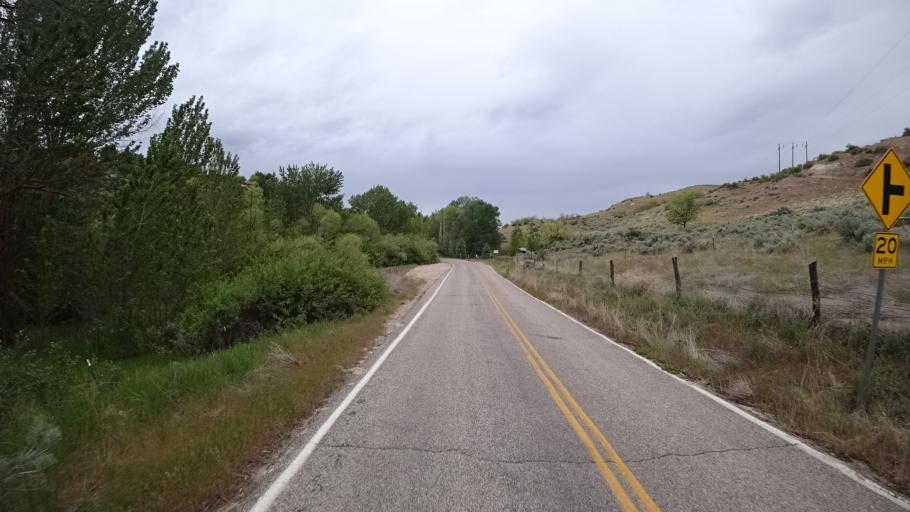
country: US
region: Idaho
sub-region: Ada County
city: Boise
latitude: 43.6163
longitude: -116.1578
